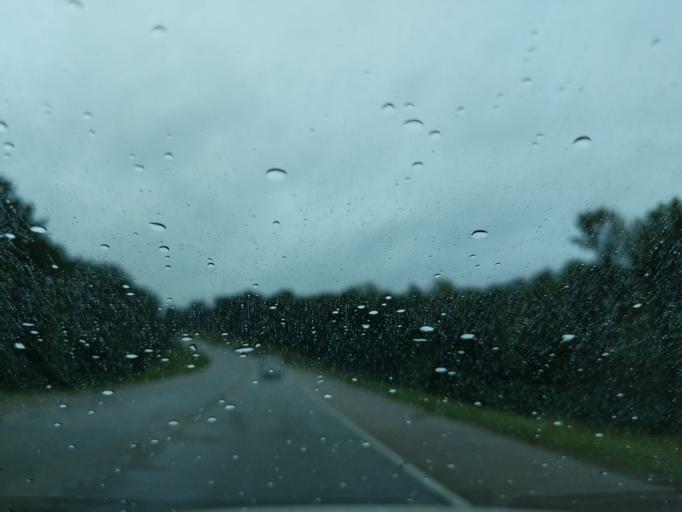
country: US
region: Louisiana
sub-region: Webster Parish
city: Minden
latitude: 32.5987
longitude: -93.2498
